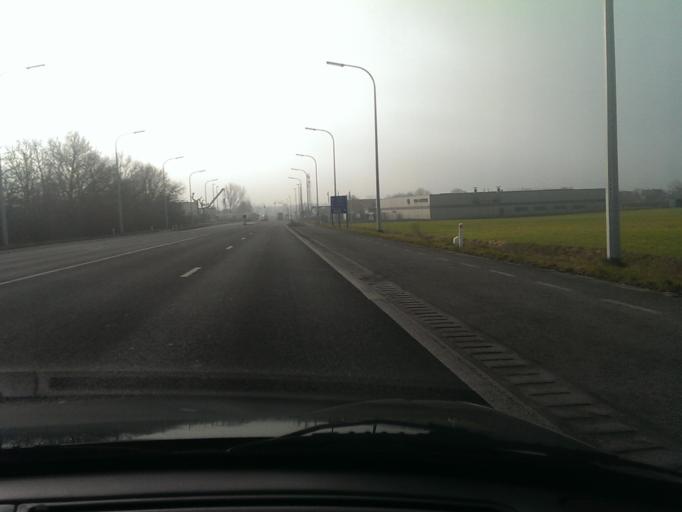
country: BE
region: Flanders
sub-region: Provincie West-Vlaanderen
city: Roeselare
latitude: 50.9364
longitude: 3.1004
